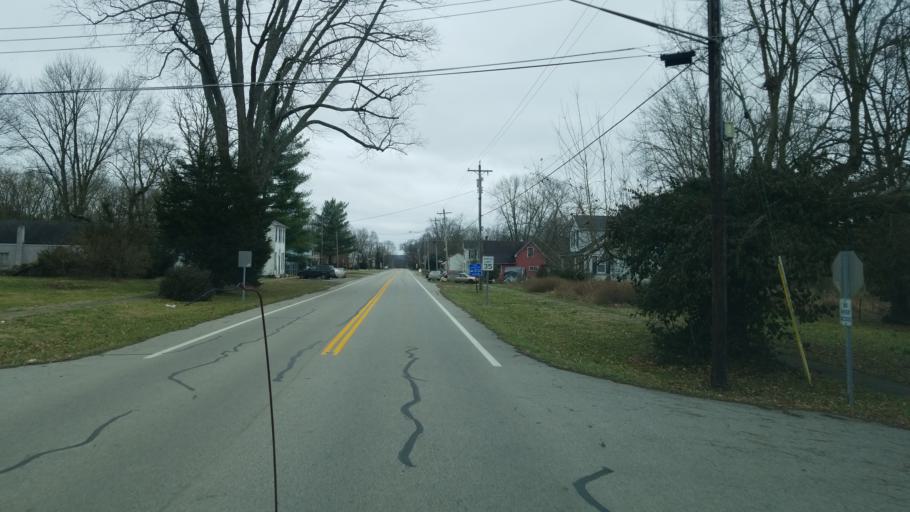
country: US
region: Ohio
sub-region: Clermont County
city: New Richmond
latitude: 38.8102
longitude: -84.2126
